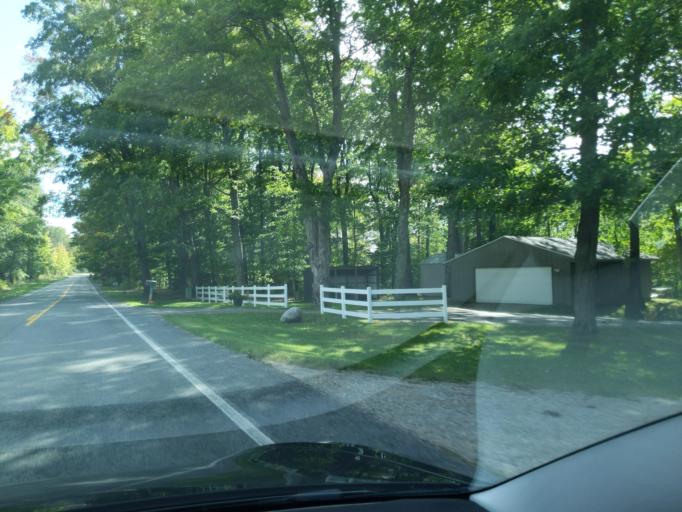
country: US
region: Michigan
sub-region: Antrim County
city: Bellaire
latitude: 44.9926
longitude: -85.2866
